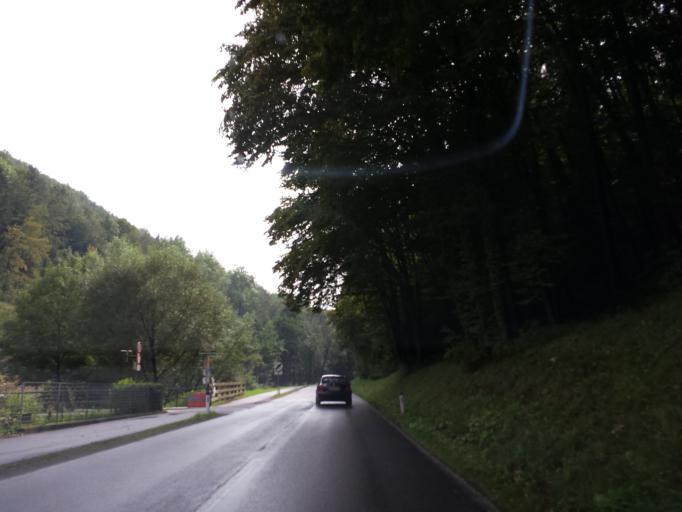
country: AT
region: Styria
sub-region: Politischer Bezirk Graz-Umgebung
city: Thal
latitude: 47.0860
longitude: 15.3710
